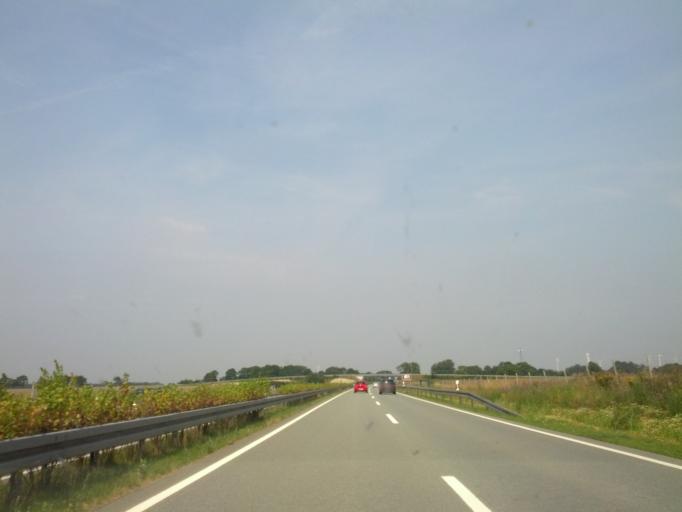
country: DE
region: Mecklenburg-Vorpommern
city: Wittenhagen
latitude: 54.1380
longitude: 13.1605
